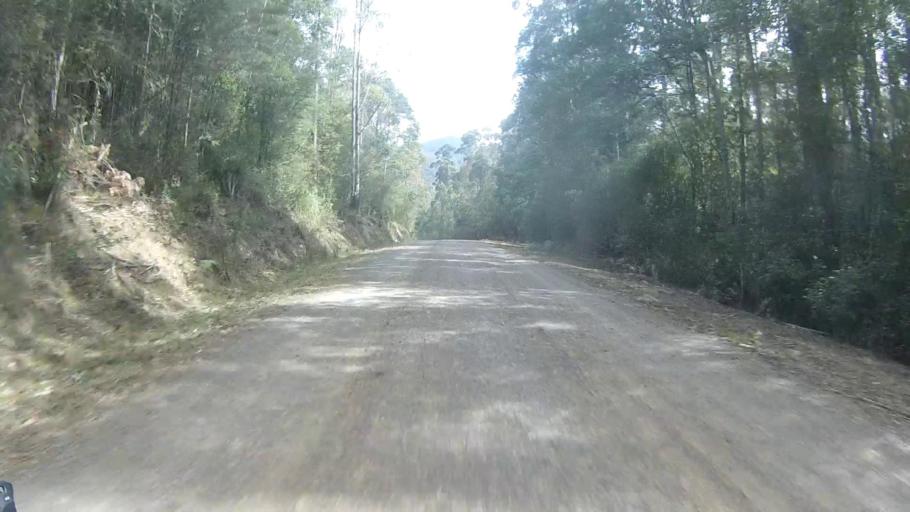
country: AU
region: Tasmania
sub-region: Sorell
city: Sorell
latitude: -42.7138
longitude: 147.8409
